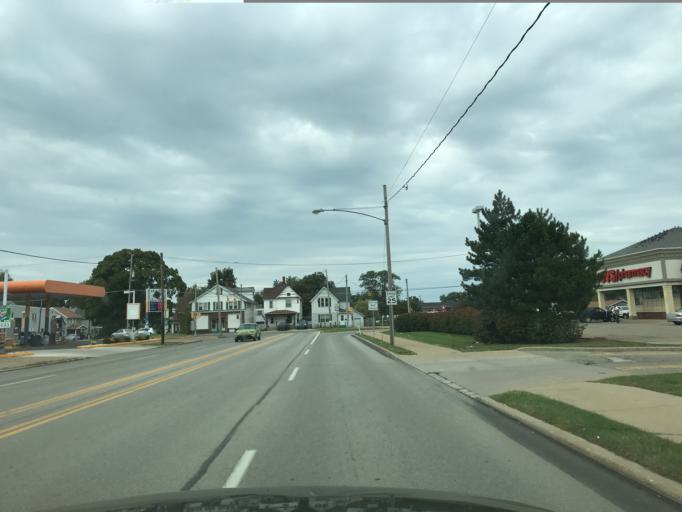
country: US
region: Pennsylvania
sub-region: Erie County
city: Wesleyville
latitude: 42.1275
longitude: -80.0442
